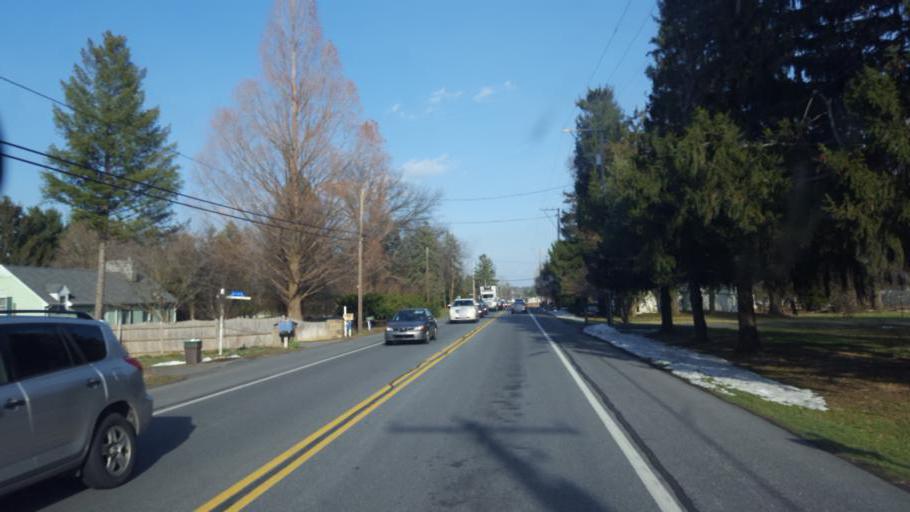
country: US
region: Pennsylvania
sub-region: Lancaster County
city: Brownstown
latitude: 40.0806
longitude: -76.2462
